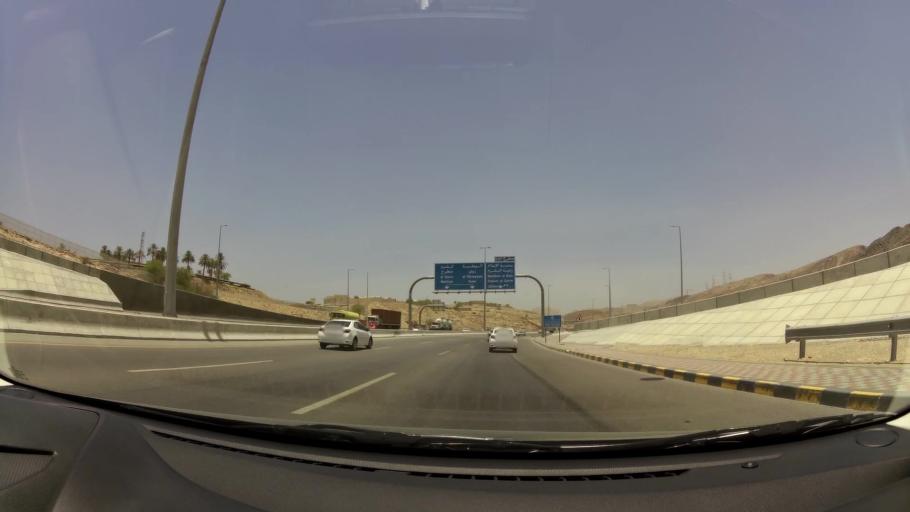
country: OM
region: Muhafazat Masqat
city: Bawshar
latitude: 23.5983
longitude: 58.4798
